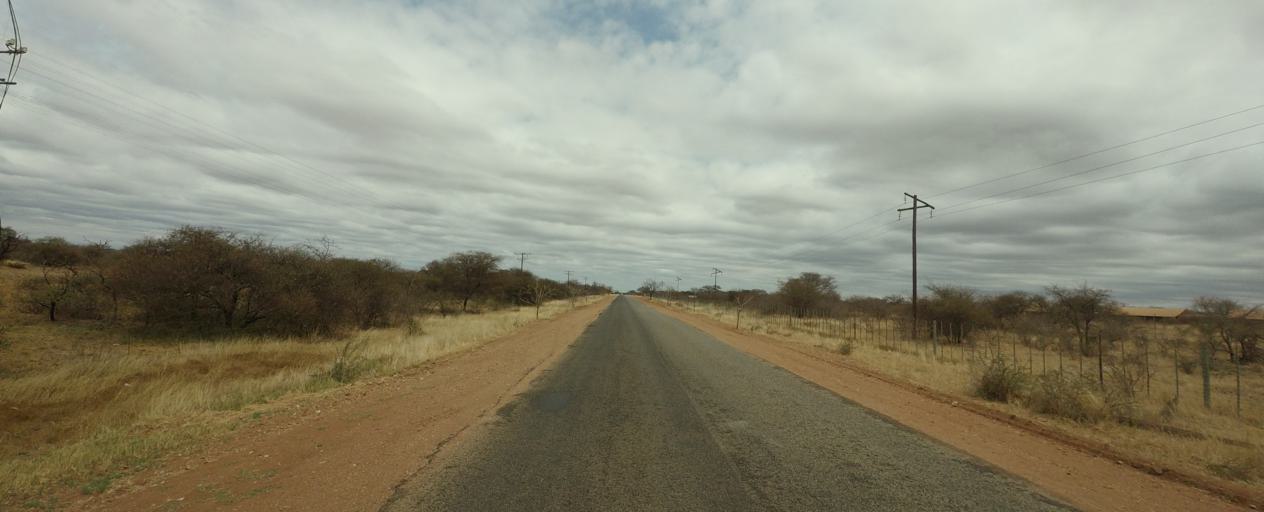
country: BW
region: Central
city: Mathathane
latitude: -22.6774
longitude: 29.1004
